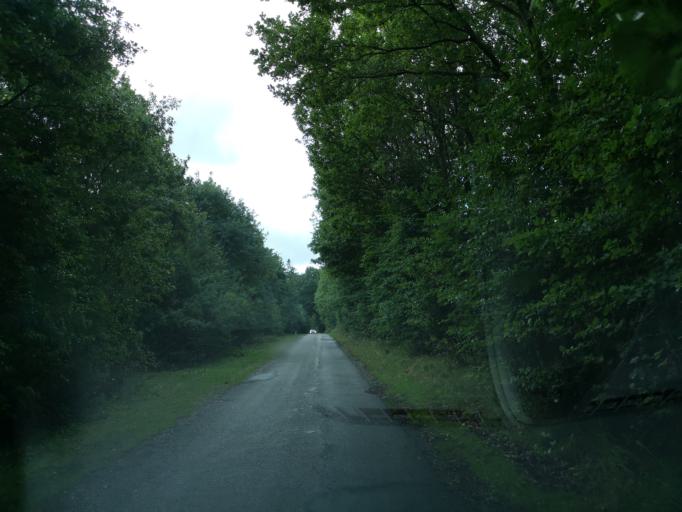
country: DK
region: Central Jutland
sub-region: Holstebro Kommune
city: Holstebro
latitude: 56.3371
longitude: 8.6390
